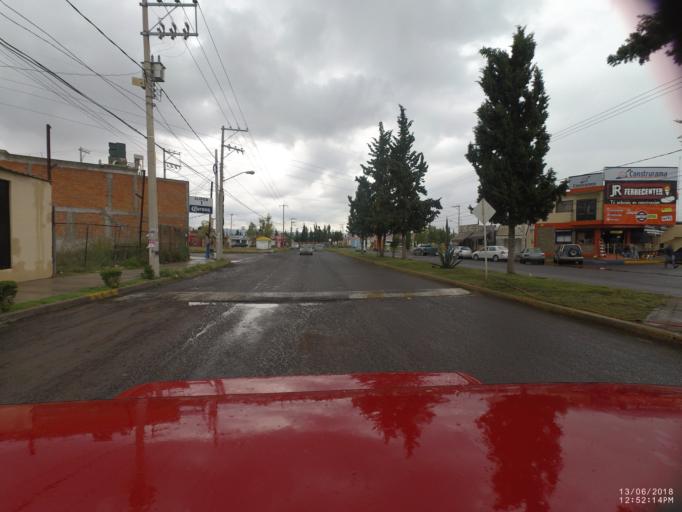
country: MX
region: Aguascalientes
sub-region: Jesus Maria
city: Arboledas Paso Blanco [Fraccionamiento]
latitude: 21.9683
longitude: -102.2978
